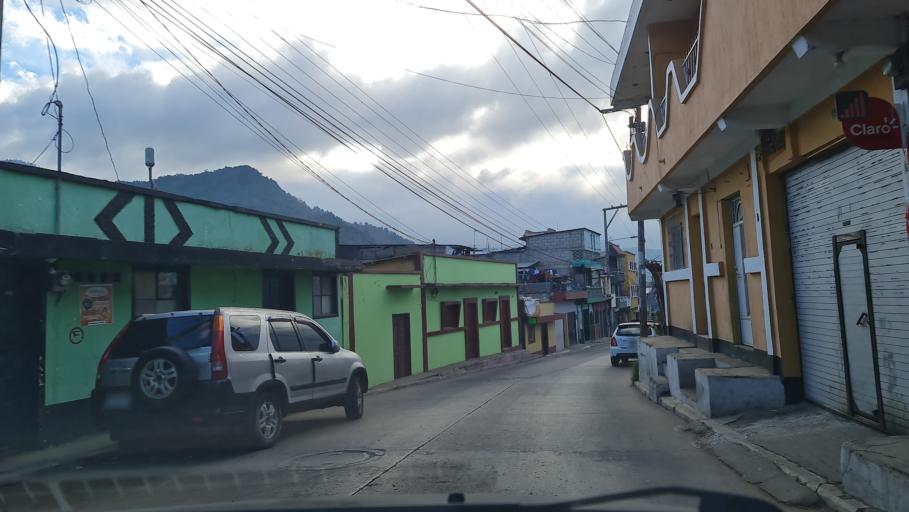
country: GT
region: San Marcos
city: San Pedro Sacatepequez
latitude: 14.9739
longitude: -91.7782
